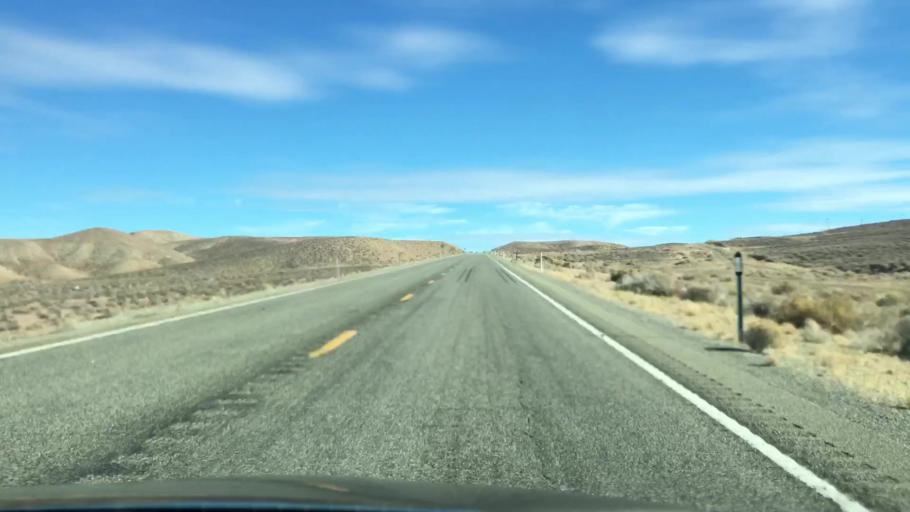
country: US
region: Nevada
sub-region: Lyon County
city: Yerington
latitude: 39.0460
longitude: -118.9675
